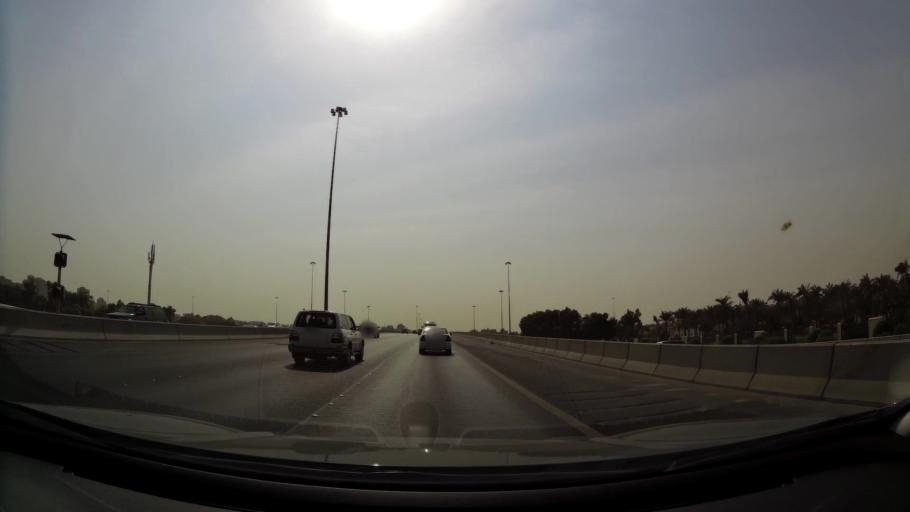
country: KW
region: Al Asimah
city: Ar Rabiyah
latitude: 29.2916
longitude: 47.9471
